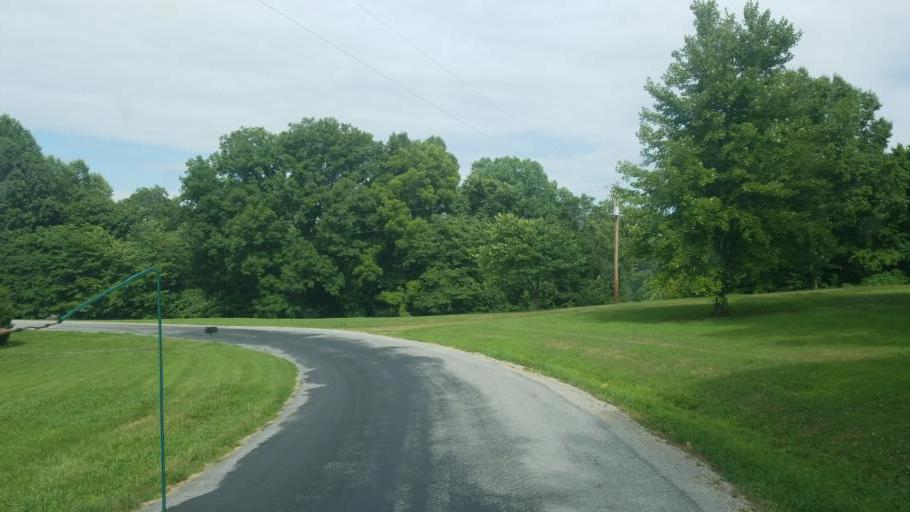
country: US
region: Illinois
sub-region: Union County
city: Cobden
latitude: 37.6118
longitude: -89.3438
